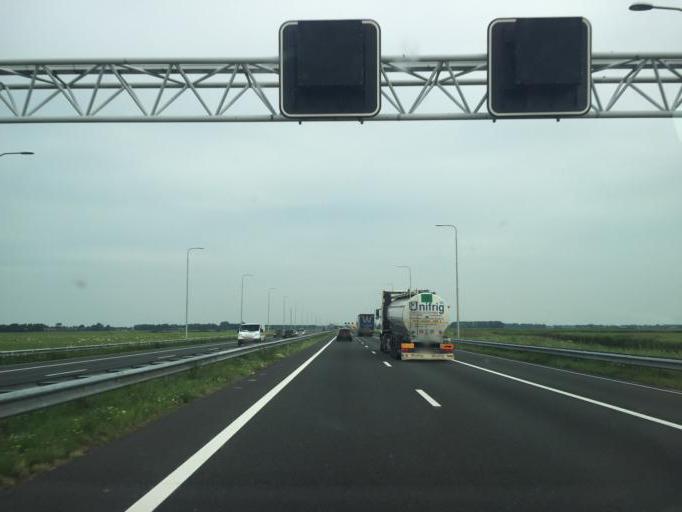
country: NL
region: North Holland
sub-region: Gemeente Uitgeest
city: Uitgeest
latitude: 52.5616
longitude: 4.7175
